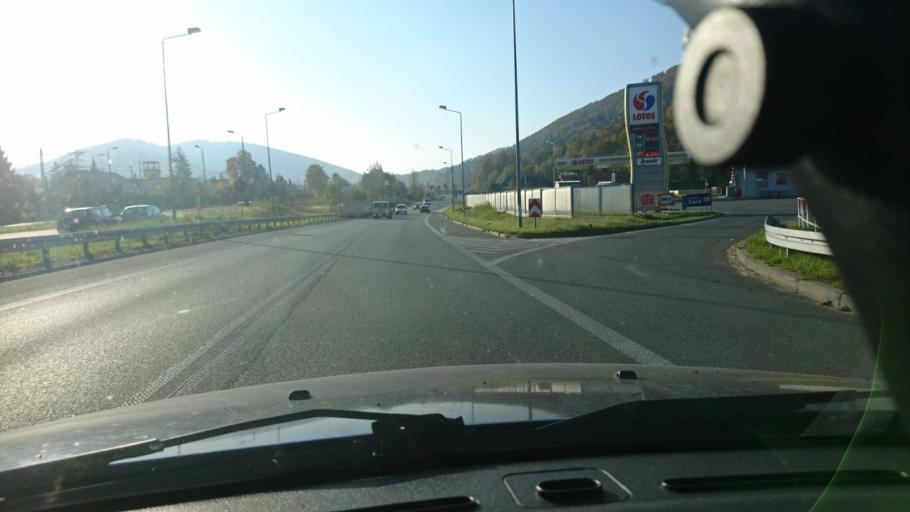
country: PL
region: Silesian Voivodeship
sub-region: Powiat cieszynski
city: Ustron
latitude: 49.6957
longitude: 18.8302
